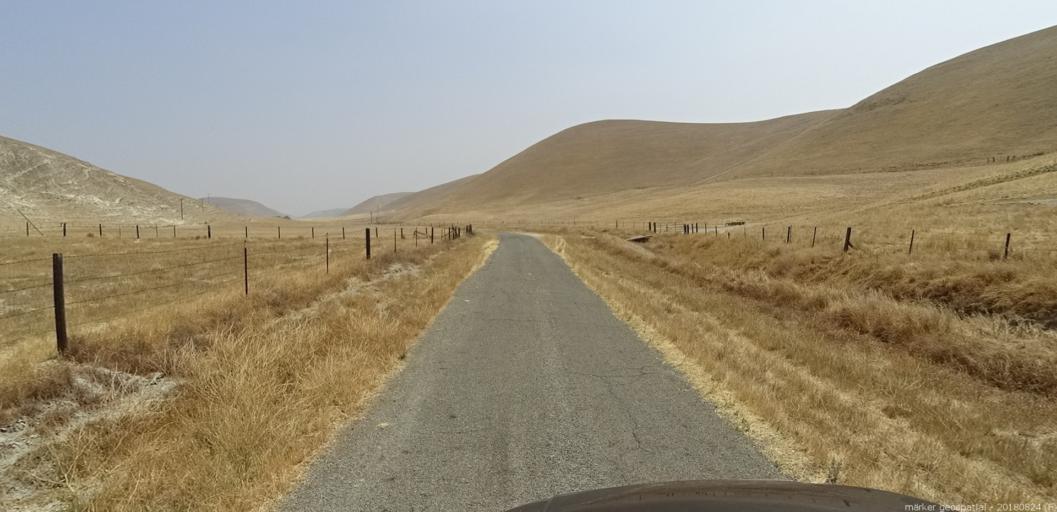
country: US
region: California
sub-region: Monterey County
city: King City
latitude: 36.1909
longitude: -120.9761
